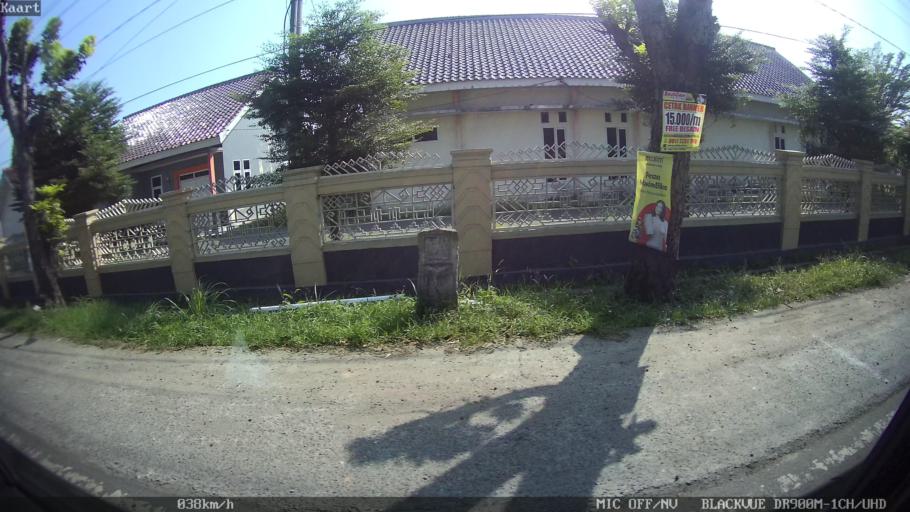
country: ID
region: Lampung
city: Natar
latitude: -5.2478
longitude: 105.1796
